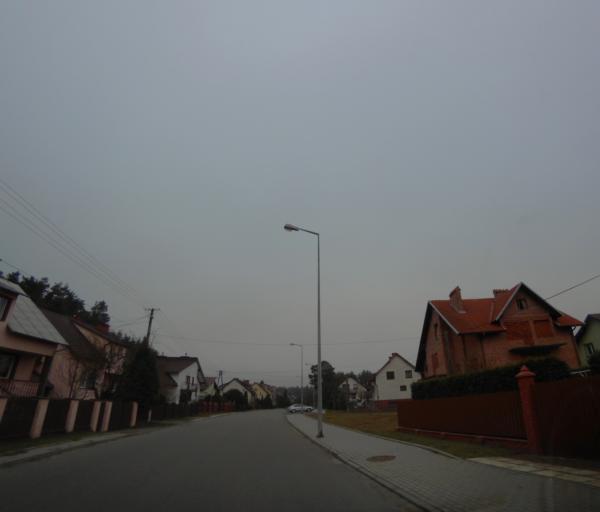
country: PL
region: Subcarpathian Voivodeship
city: Nowa Sarzyna
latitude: 50.3146
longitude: 22.3425
